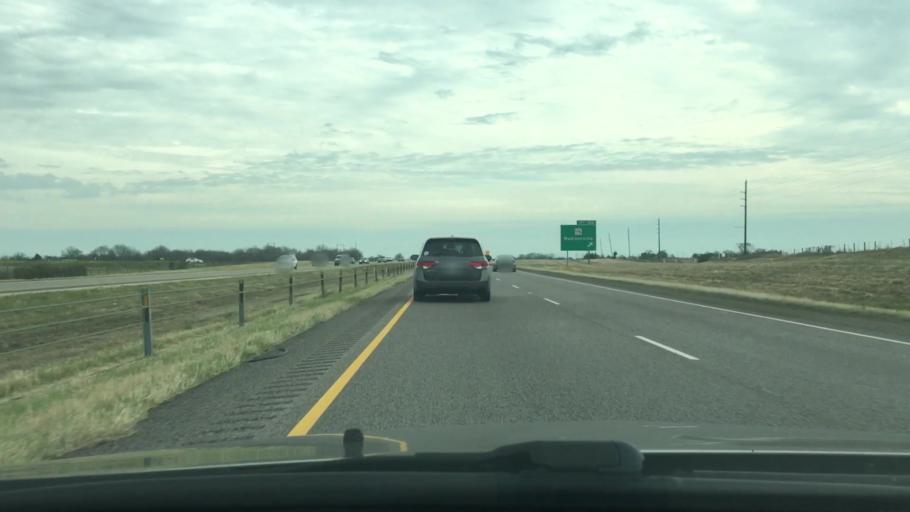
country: US
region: Texas
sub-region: Madison County
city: Madisonville
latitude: 31.0211
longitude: -95.9281
